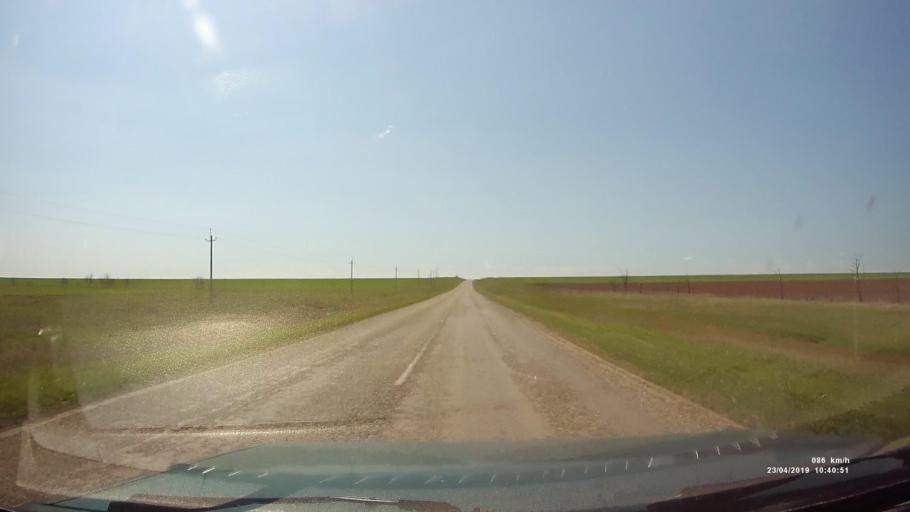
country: RU
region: Kalmykiya
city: Yashalta
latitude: 46.5010
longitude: 42.6384
